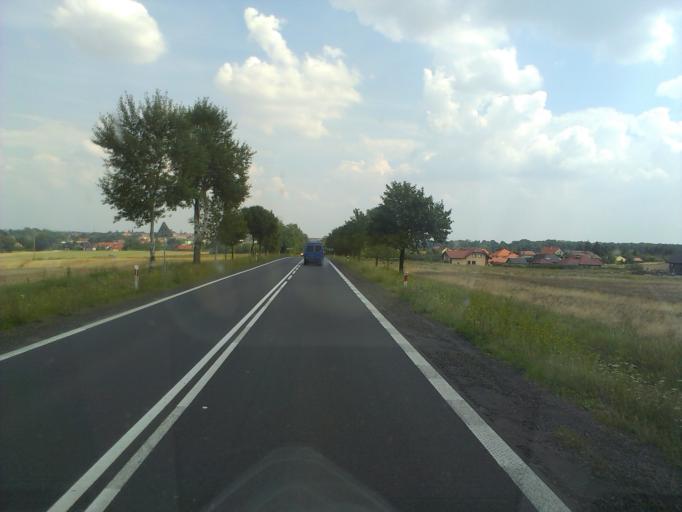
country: PL
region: Lower Silesian Voivodeship
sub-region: Powiat sredzki
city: Sroda Slaska
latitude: 51.1651
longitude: 16.5679
